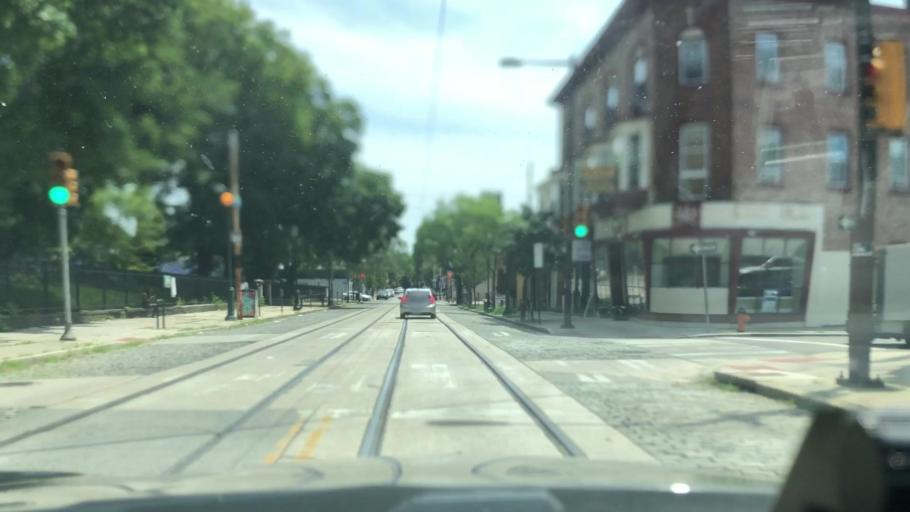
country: US
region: Pennsylvania
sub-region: Montgomery County
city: Wyndmoor
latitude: 40.0394
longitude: -75.1778
